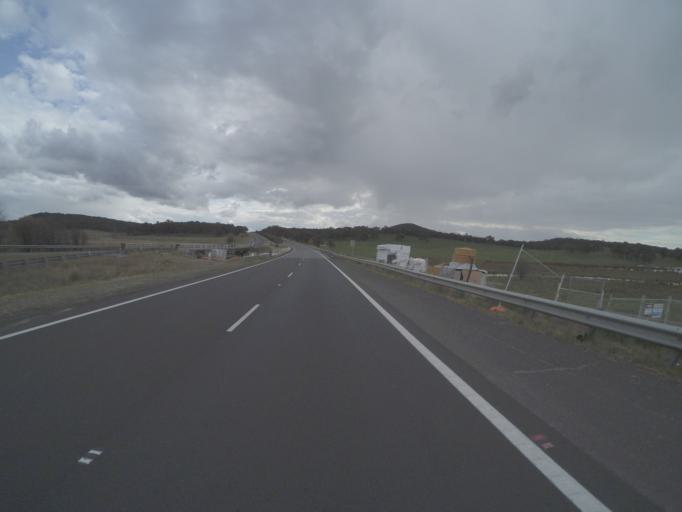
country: AU
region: New South Wales
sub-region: Goulburn Mulwaree
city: Goulburn
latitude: -34.7413
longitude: 149.9131
